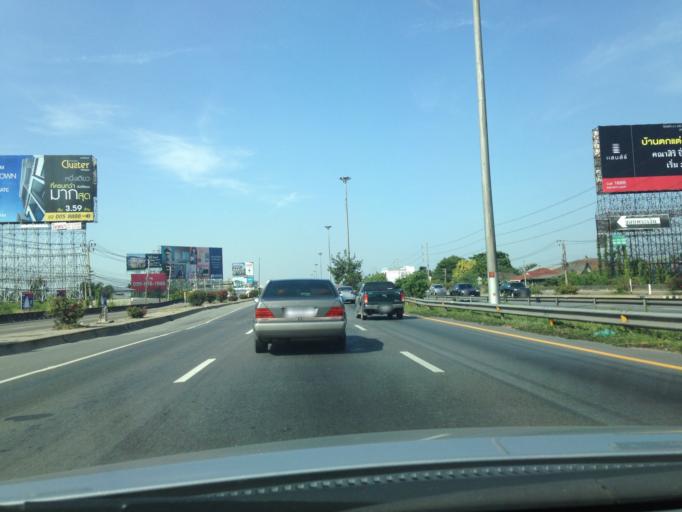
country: TH
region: Nonthaburi
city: Bang Yai
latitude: 13.8382
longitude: 100.4132
